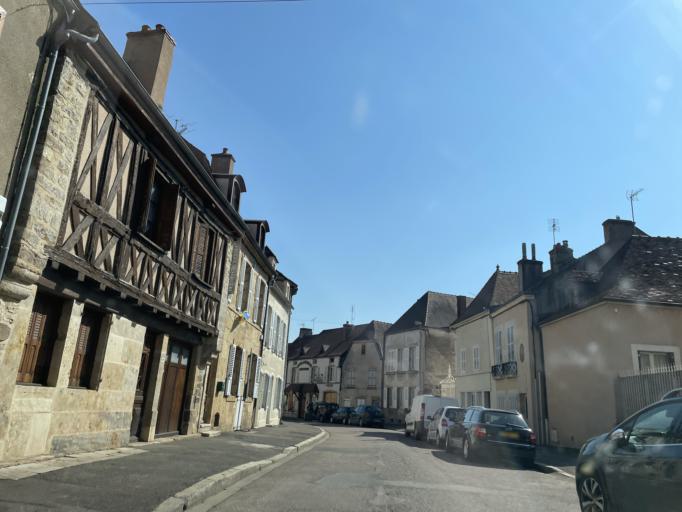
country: FR
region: Bourgogne
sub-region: Departement de la Cote-d'Or
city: Semur-en-Auxois
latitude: 47.4893
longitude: 4.3342
